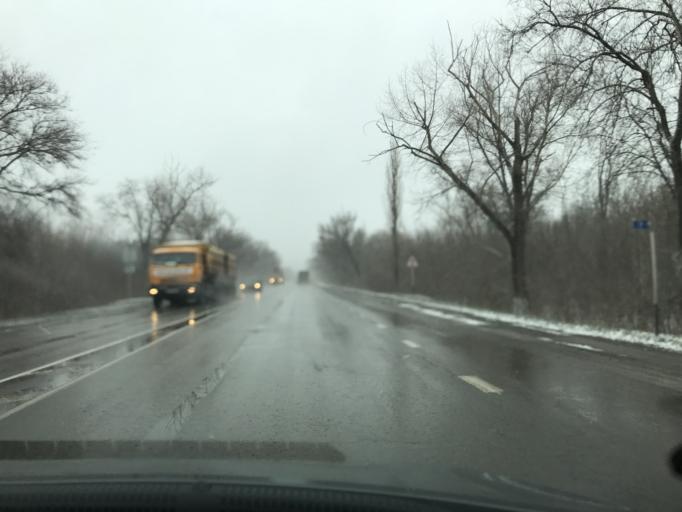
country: RU
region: Rostov
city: Bataysk
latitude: 47.0472
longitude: 39.8444
